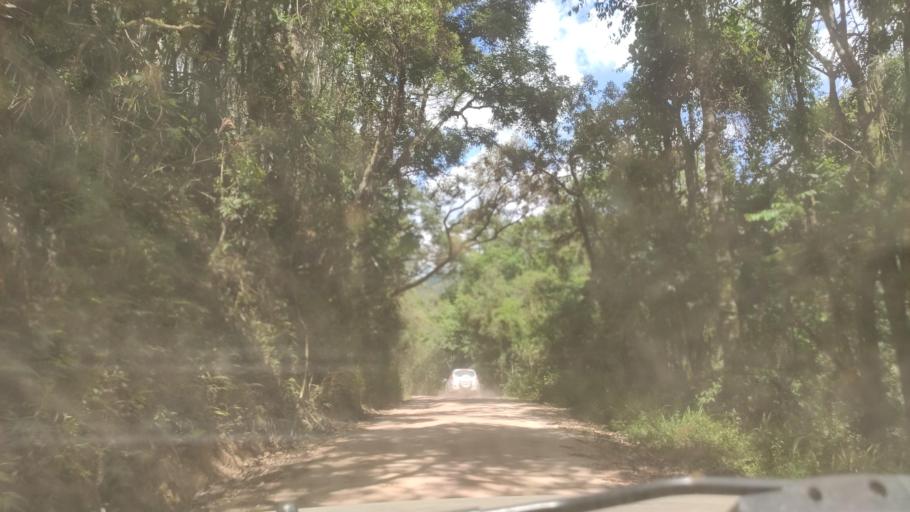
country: BR
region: Minas Gerais
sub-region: Camanducaia
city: Camanducaia
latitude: -22.7707
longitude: -46.0044
